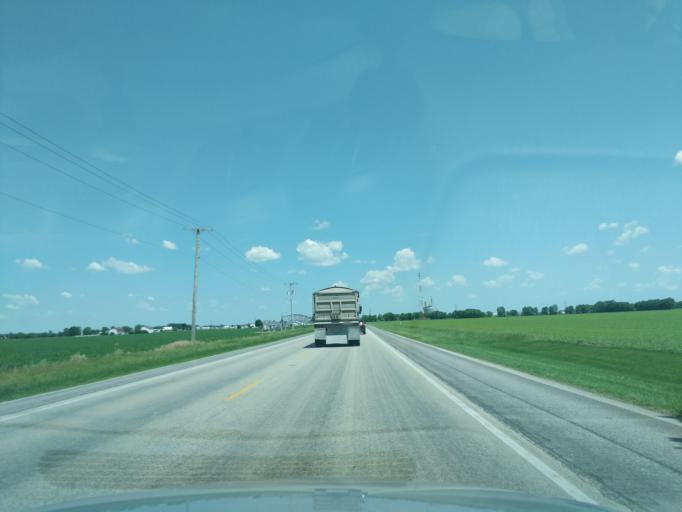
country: US
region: Indiana
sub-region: LaGrange County
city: Topeka
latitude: 41.5269
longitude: -85.5778
